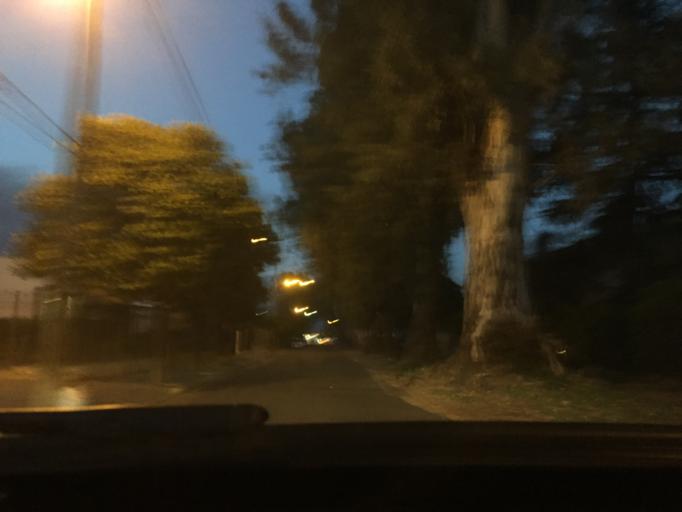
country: AR
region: Cordoba
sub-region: Departamento de Capital
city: Cordoba
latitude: -31.3748
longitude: -64.2246
